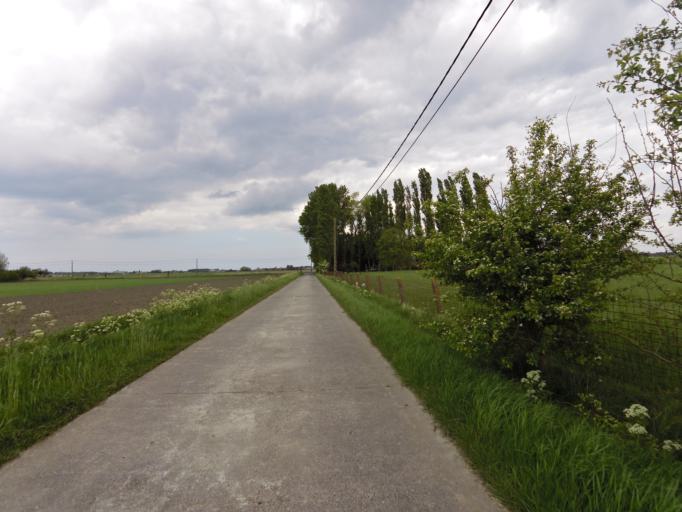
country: BE
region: Flanders
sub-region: Provincie West-Vlaanderen
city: Middelkerke
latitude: 51.1458
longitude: 2.8311
